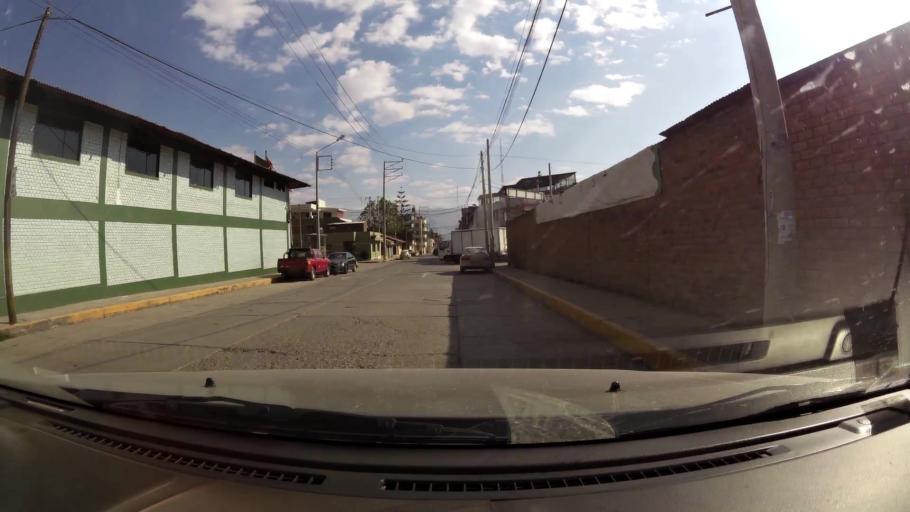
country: PE
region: Junin
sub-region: Provincia de Huancayo
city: Huancayo
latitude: -12.0614
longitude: -75.2112
